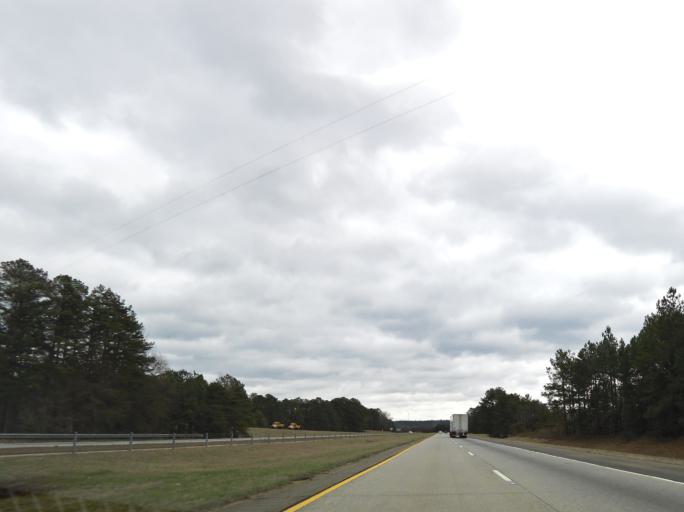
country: US
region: Georgia
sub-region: Twiggs County
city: Jeffersonville
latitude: 32.6580
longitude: -83.4475
